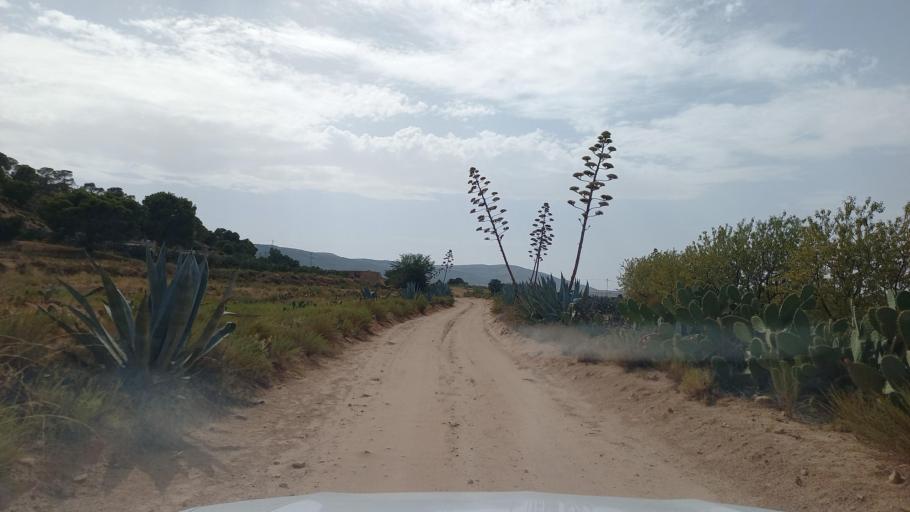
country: TN
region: Al Qasrayn
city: Kasserine
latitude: 35.3506
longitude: 8.8756
